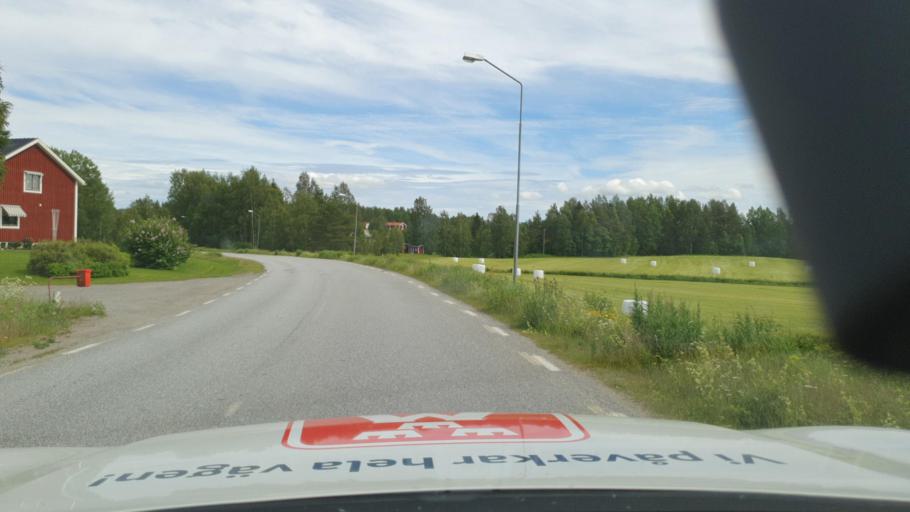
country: SE
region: Vaesterbotten
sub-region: Skelleftea Kommun
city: Viken
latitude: 64.5199
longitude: 20.9598
